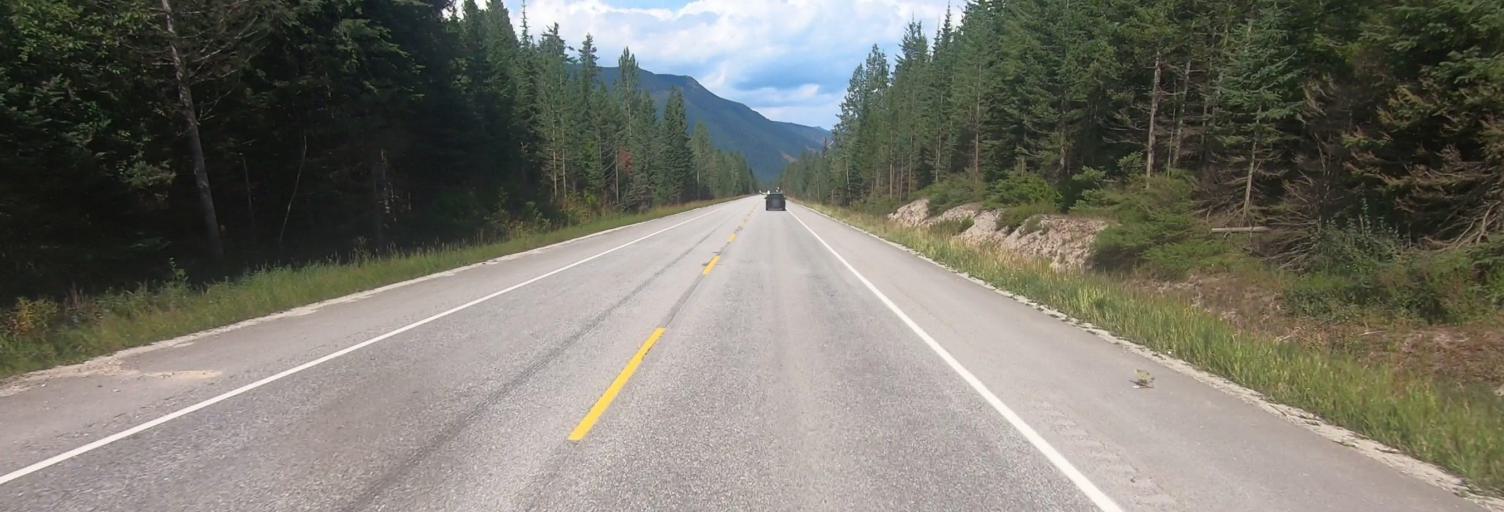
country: CA
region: British Columbia
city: Golden
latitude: 51.5000
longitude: -117.4091
